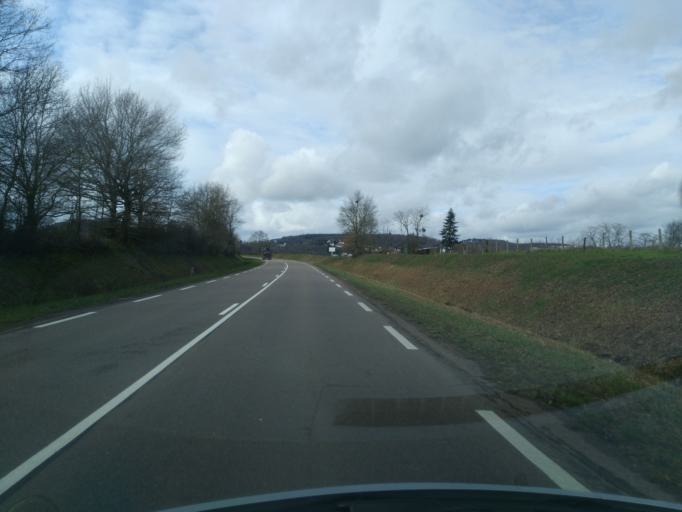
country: FR
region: Bourgogne
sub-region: Departement de Saone-et-Loire
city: Le Creusot
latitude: 46.7805
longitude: 4.4165
